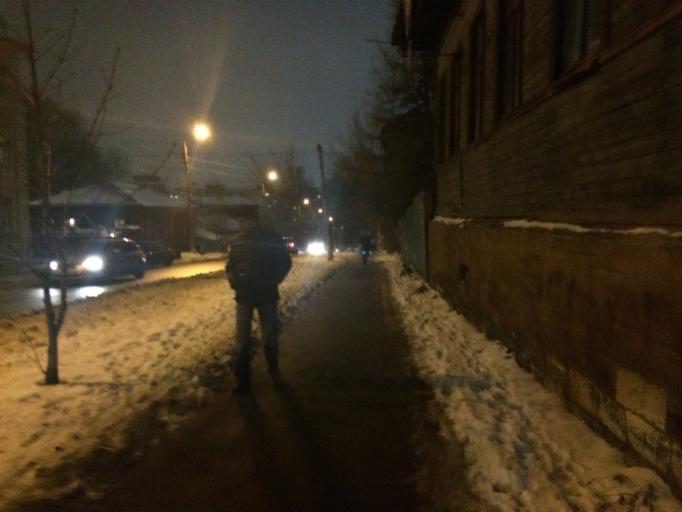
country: RU
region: Tula
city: Tula
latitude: 54.1883
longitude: 37.6021
